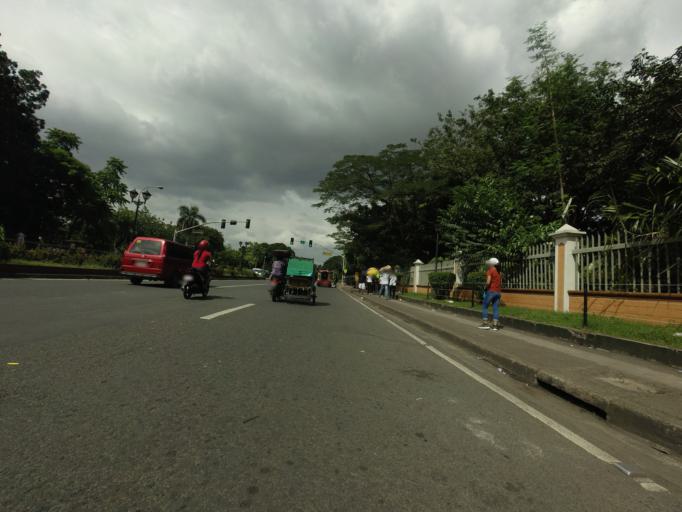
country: PH
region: Metro Manila
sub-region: City of Manila
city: Port Area
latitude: 14.5829
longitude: 120.9808
